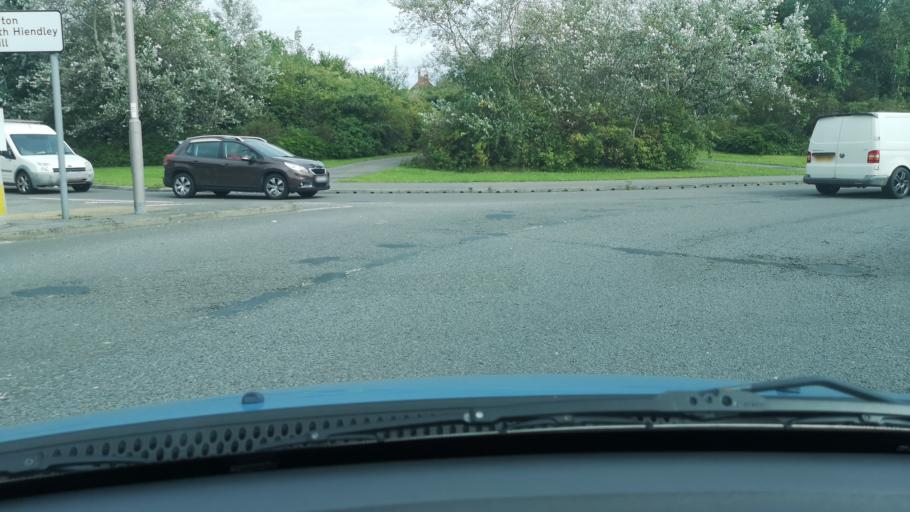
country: GB
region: England
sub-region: Barnsley
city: Shafton
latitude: 53.5885
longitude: -1.4066
